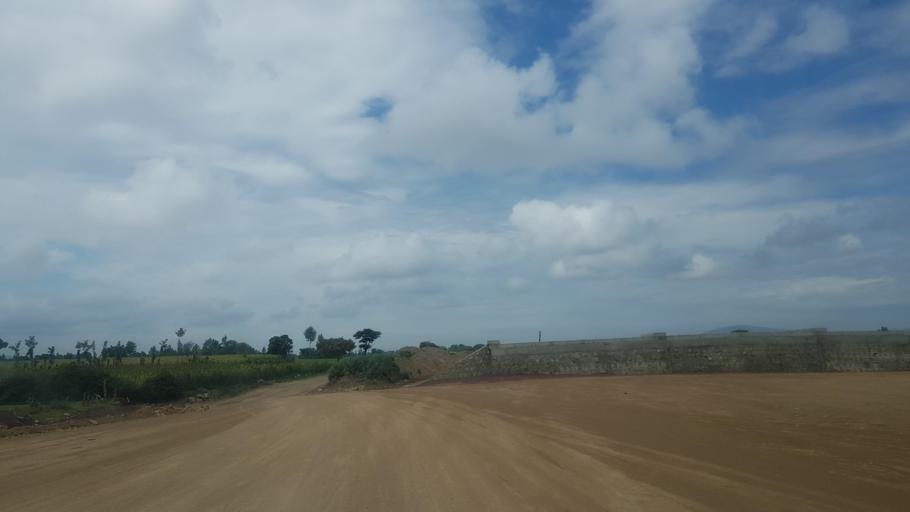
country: ET
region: Oromiya
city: Shashemene
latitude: 7.2395
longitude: 38.5791
